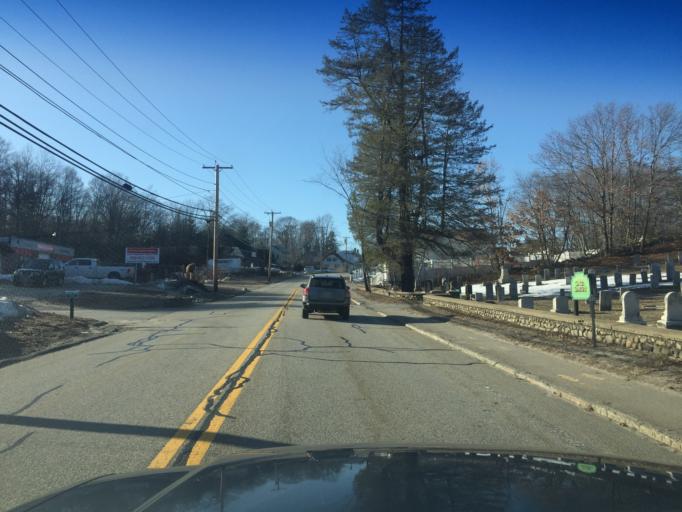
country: US
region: Massachusetts
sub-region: Norfolk County
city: Bellingham
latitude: 42.0841
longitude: -71.4706
